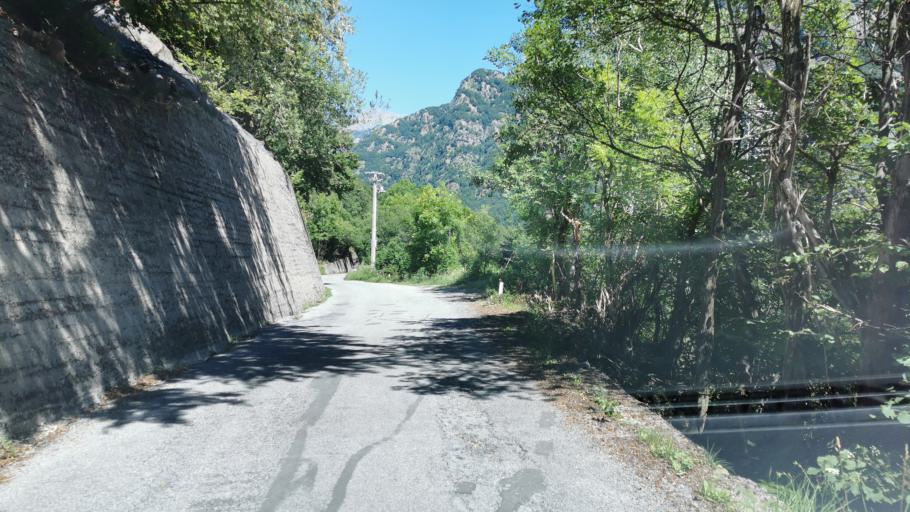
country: IT
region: Piedmont
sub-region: Provincia di Cuneo
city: Entracque
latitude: 44.2055
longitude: 7.3715
